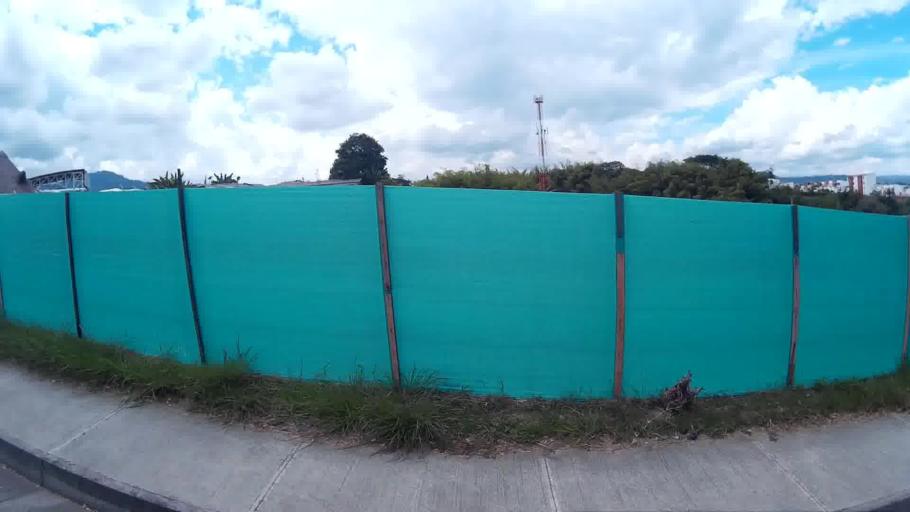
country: CO
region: Risaralda
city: Pereira
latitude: 4.8112
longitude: -75.7665
